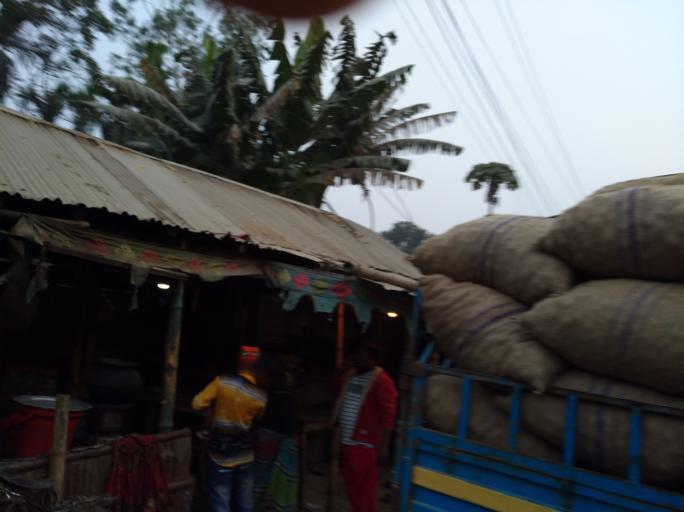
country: BD
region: Rajshahi
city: Saidpur
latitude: 25.9253
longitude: 88.8664
